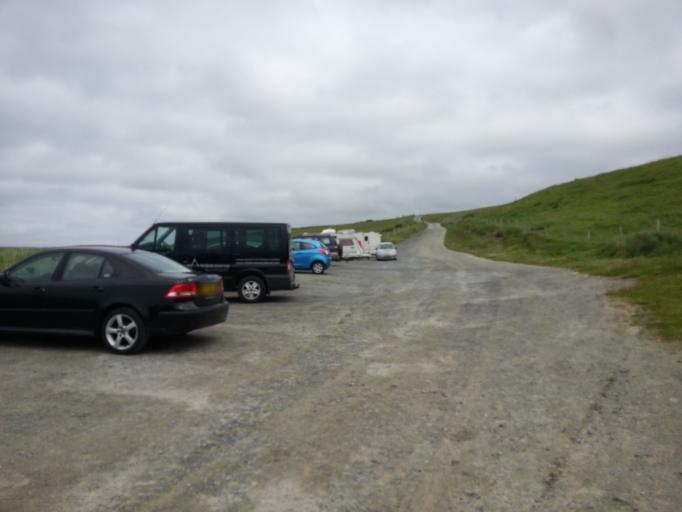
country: GB
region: Scotland
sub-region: Shetland Islands
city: Sandwick
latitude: 59.9710
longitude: -1.3307
